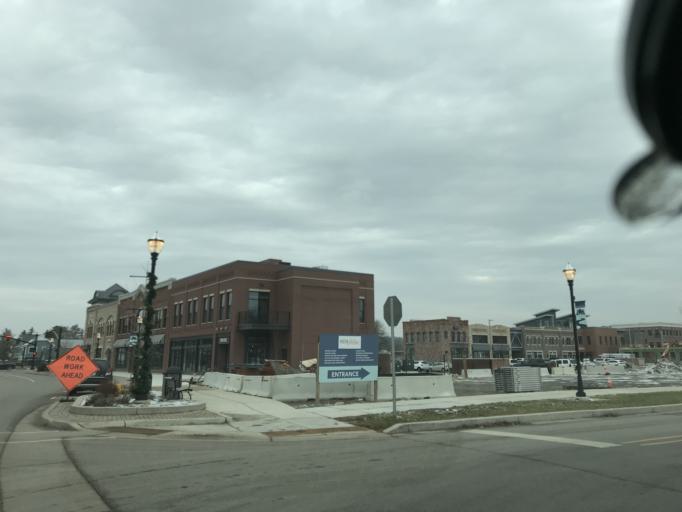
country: US
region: Michigan
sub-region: Kent County
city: Forest Hills
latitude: 42.9540
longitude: -85.4864
